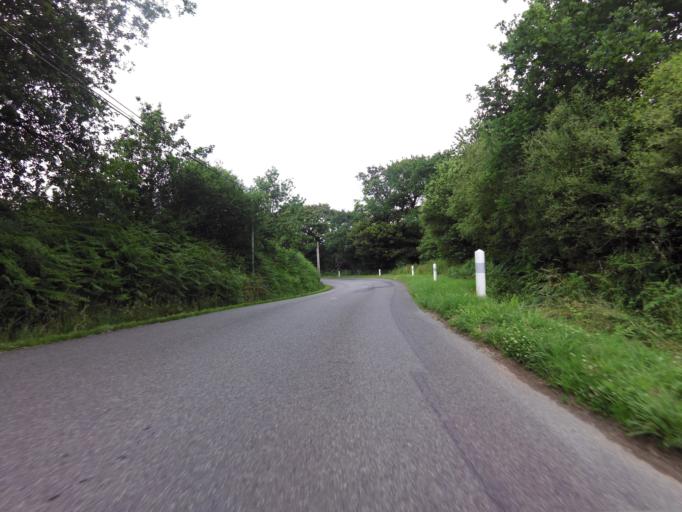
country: FR
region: Brittany
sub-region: Departement du Morbihan
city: Questembert
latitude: 47.6587
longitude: -2.4200
